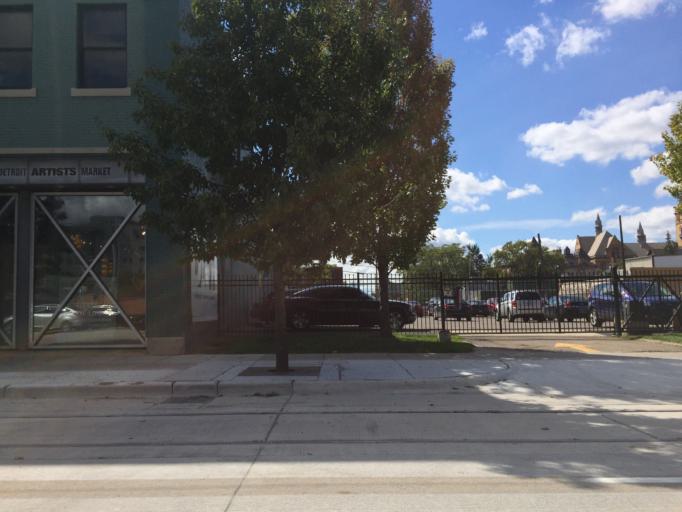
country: US
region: Michigan
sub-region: Wayne County
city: Detroit
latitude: 42.3550
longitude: -83.0633
